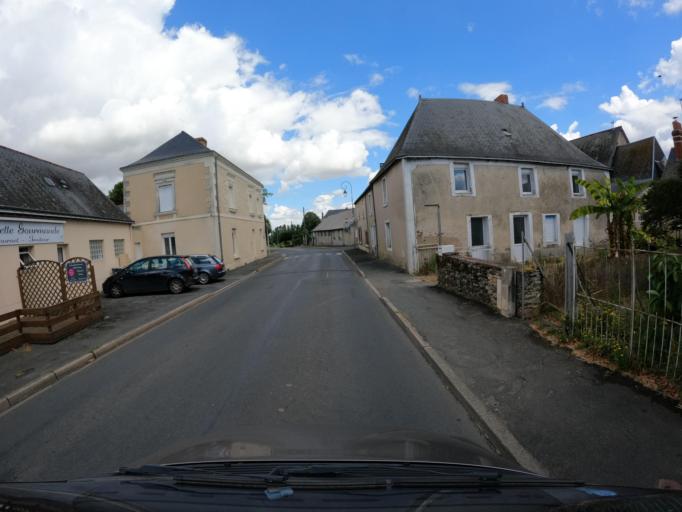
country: FR
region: Pays de la Loire
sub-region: Departement de Maine-et-Loire
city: Mire
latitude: 47.7297
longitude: -0.5171
